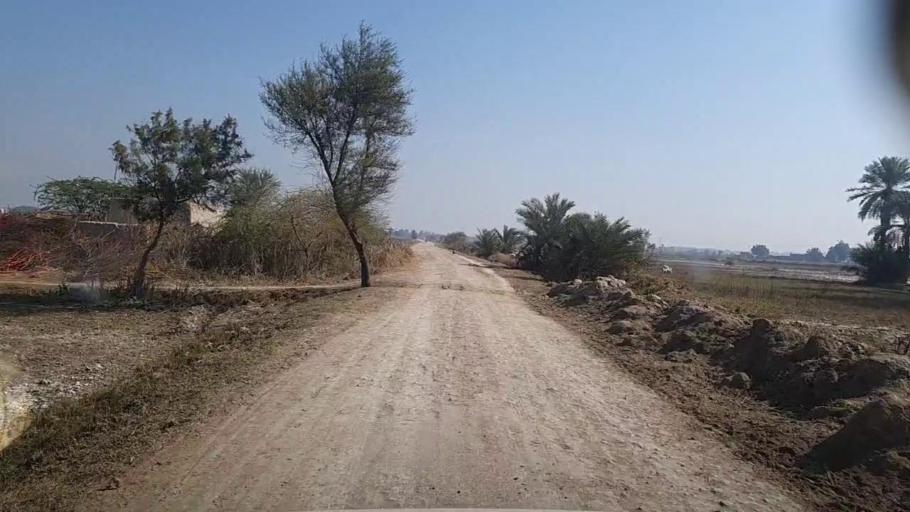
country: PK
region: Sindh
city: Khairpur
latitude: 27.9777
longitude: 69.7129
